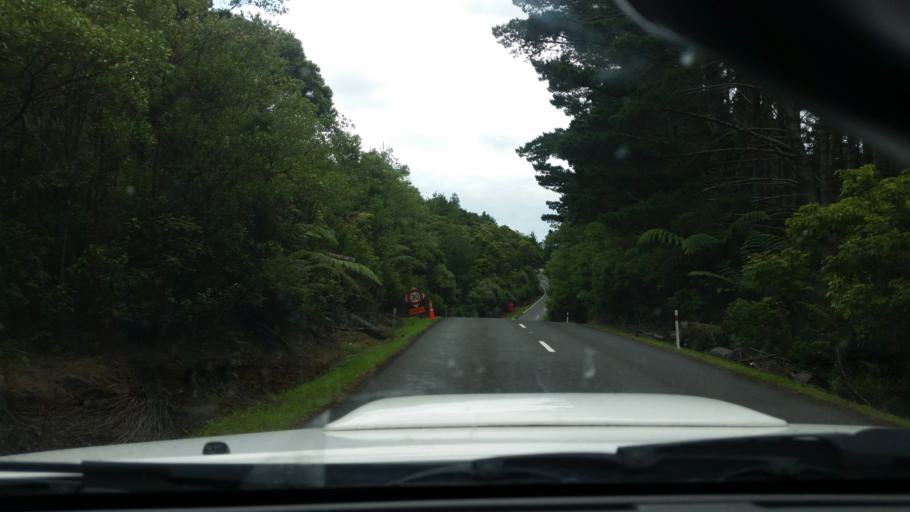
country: NZ
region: Northland
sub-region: Kaipara District
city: Dargaville
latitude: -35.7333
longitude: 173.8638
